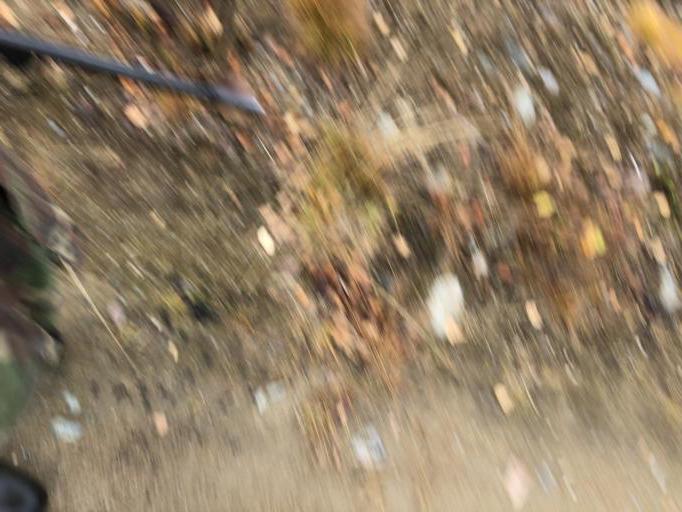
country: FI
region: Northern Ostrobothnia
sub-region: Koillismaa
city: Kuusamo
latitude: 66.5874
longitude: 29.3474
